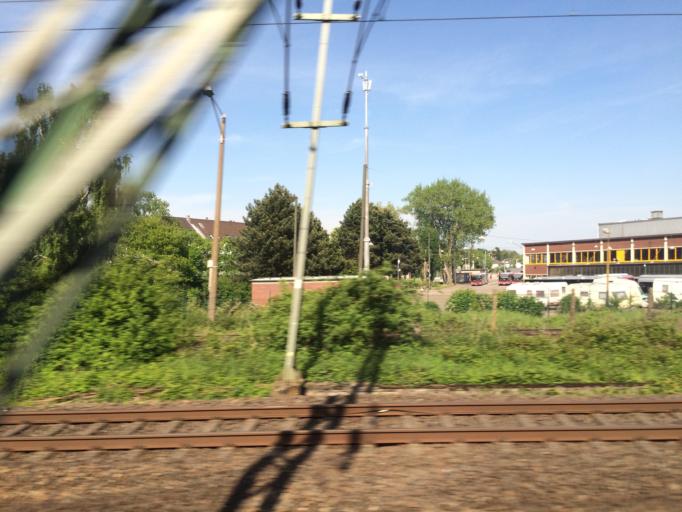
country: DE
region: North Rhine-Westphalia
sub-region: Regierungsbezirk Dusseldorf
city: Hilden
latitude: 51.1603
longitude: 6.8808
